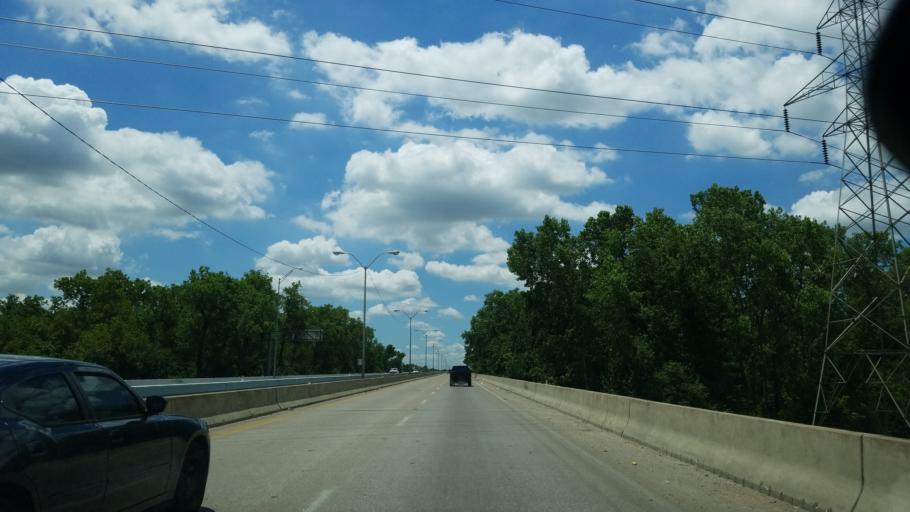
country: US
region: Texas
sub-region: Dallas County
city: Dallas
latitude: 32.7321
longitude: -96.7580
